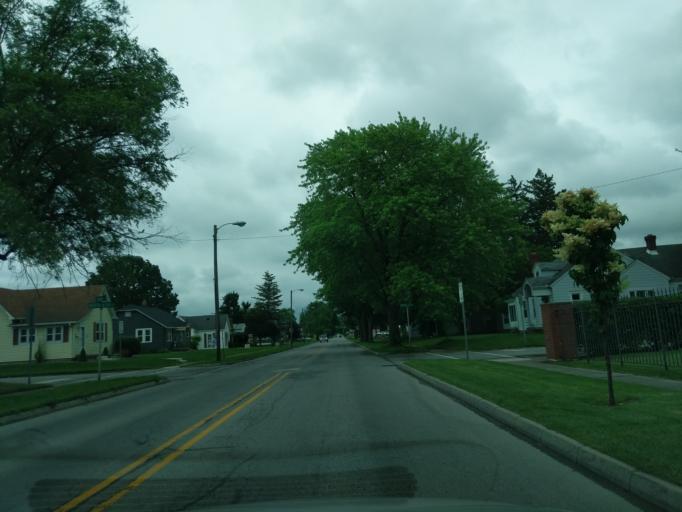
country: US
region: Indiana
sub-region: Madison County
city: Elwood
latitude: 40.2769
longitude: -85.8544
